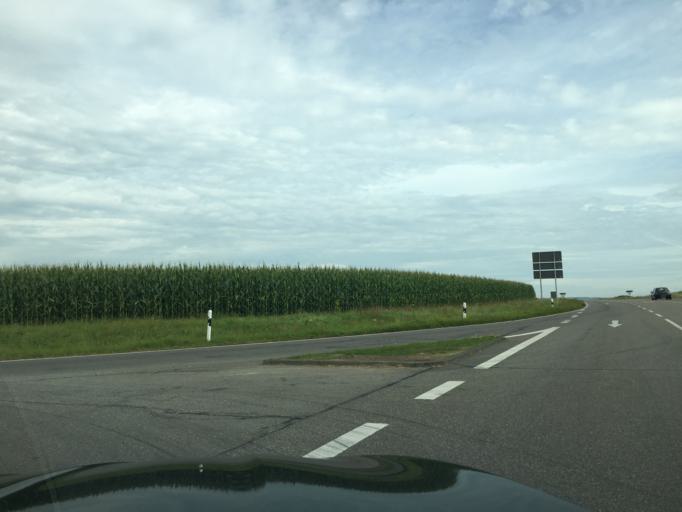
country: DE
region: Baden-Wuerttemberg
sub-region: Tuebingen Region
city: Emeringen
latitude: 48.2050
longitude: 9.5321
